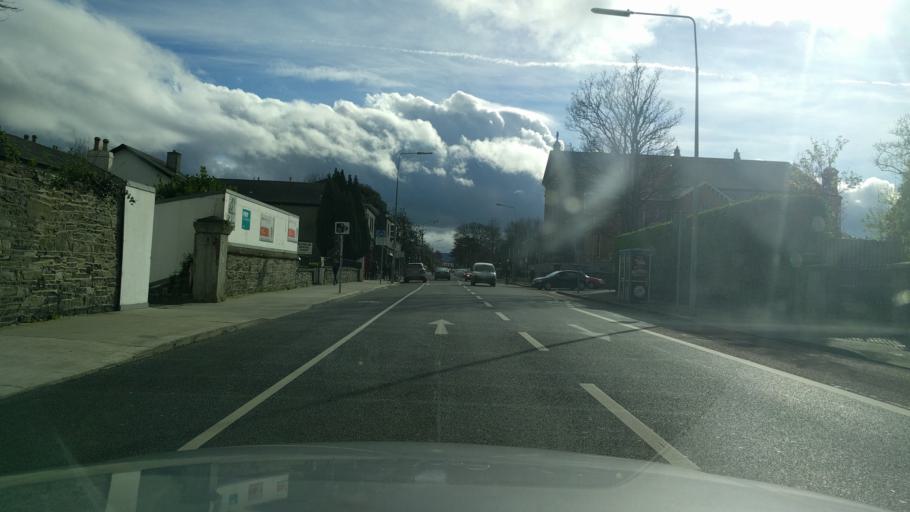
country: IE
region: Leinster
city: Rathgar
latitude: 53.3180
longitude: -6.2697
